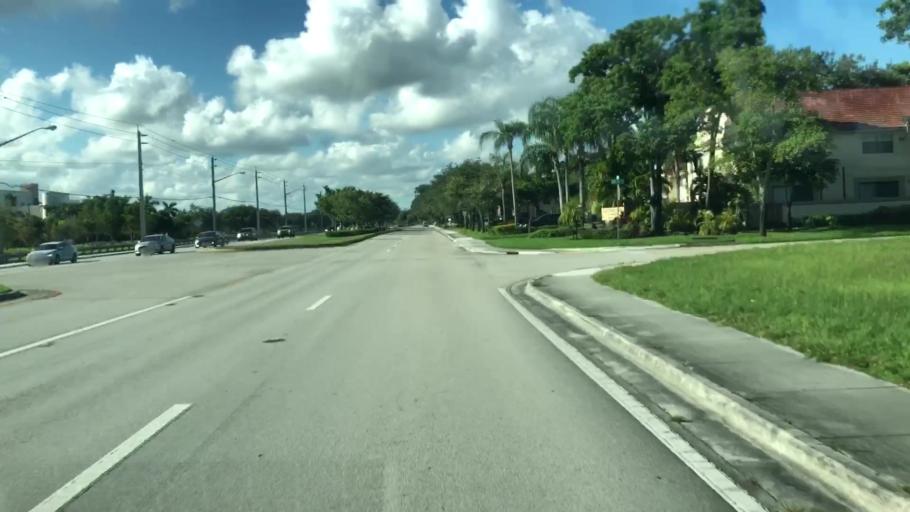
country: US
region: Florida
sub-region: Broward County
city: Coral Springs
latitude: 26.2661
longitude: -80.2663
